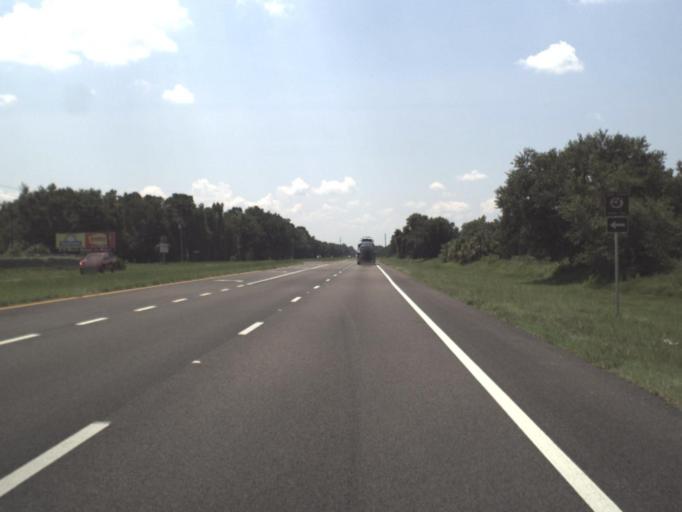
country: US
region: Florida
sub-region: Levy County
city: Inglis
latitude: 29.0044
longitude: -82.6580
